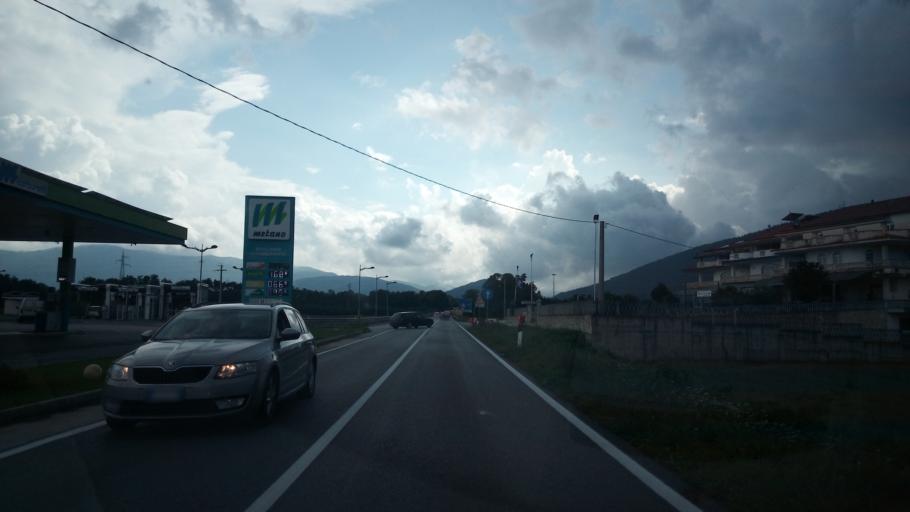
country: IT
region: Campania
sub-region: Provincia di Salerno
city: Buonabitacolo
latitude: 40.2888
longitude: 15.6402
